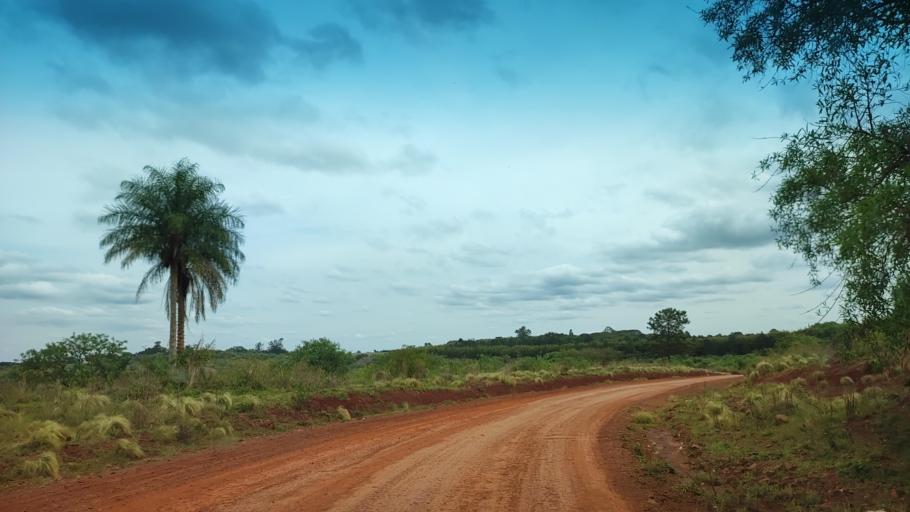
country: AR
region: Misiones
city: Garupa
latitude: -27.5150
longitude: -55.9710
